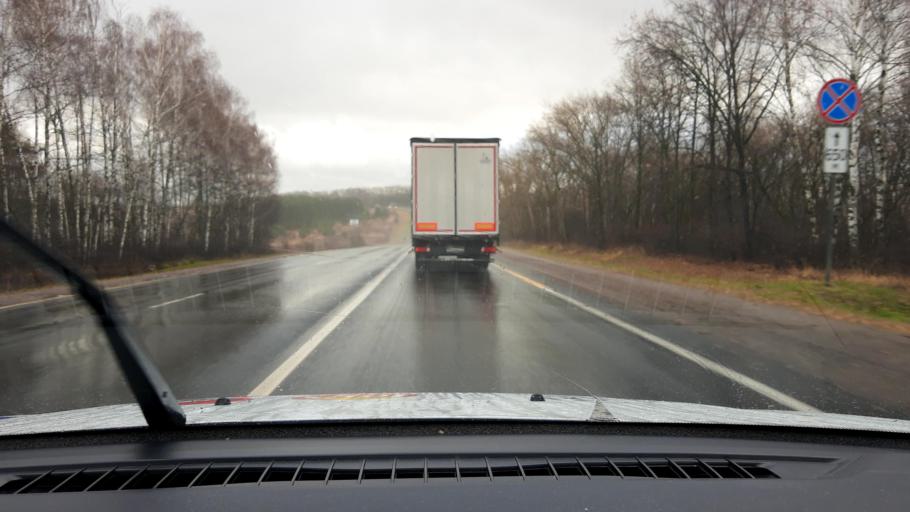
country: RU
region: Nizjnij Novgorod
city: Pamyat' Parizhskoy Kommuny
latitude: 56.0499
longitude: 44.4143
